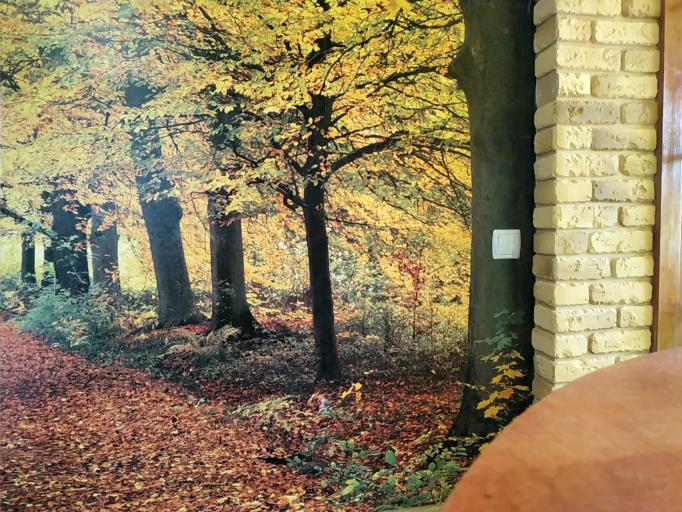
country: RU
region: Pskov
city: Dno
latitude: 57.9119
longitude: 30.1715
